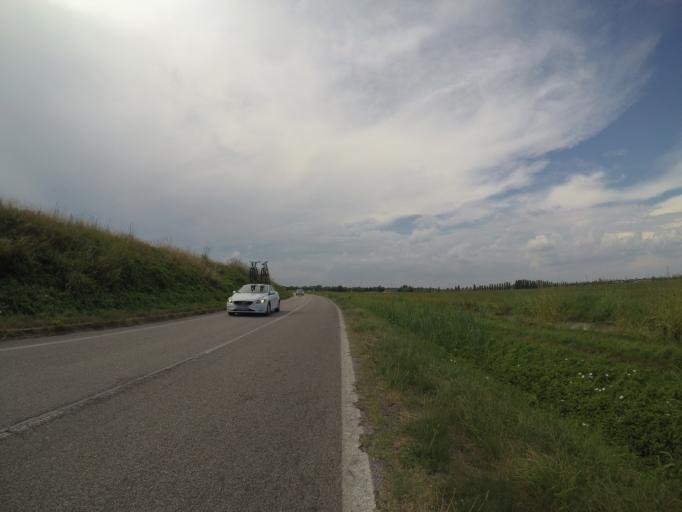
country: IT
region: Friuli Venezia Giulia
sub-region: Provincia di Udine
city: Pertegada
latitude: 45.6797
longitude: 13.0647
